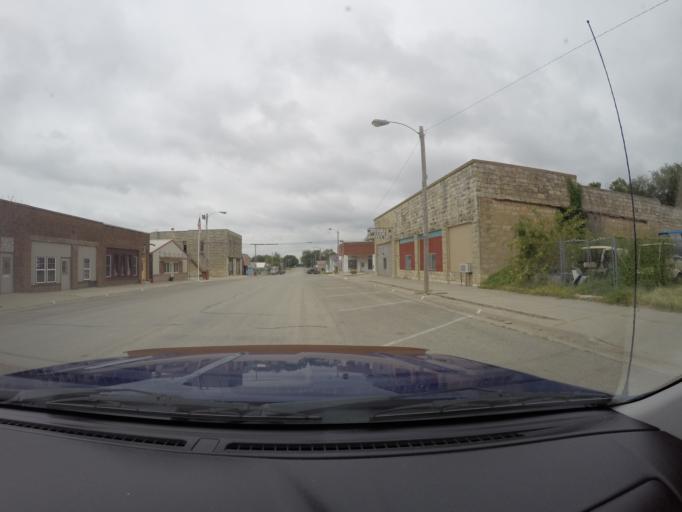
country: US
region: Kansas
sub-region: Morris County
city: Council Grove
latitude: 38.8637
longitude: -96.4897
